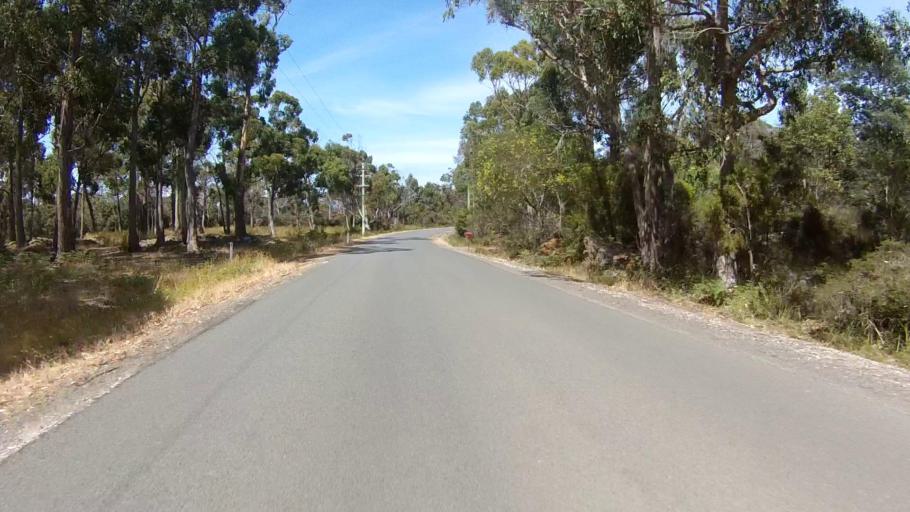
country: AU
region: Tasmania
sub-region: Huon Valley
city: Cygnet
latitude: -43.2402
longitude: 147.1238
